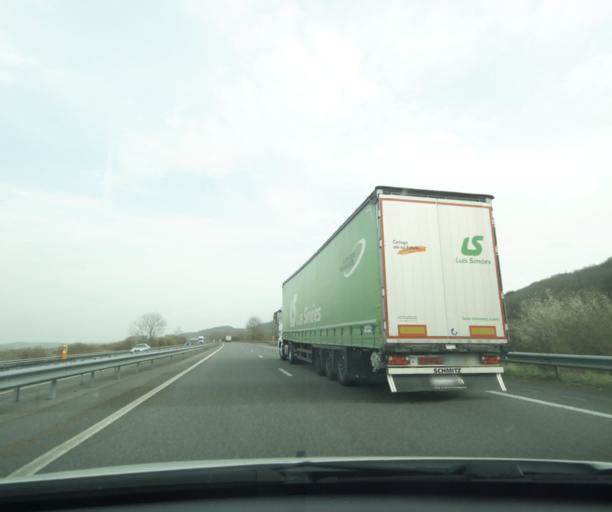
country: FR
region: Aquitaine
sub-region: Departement des Landes
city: Labatut
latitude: 43.5184
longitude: -0.9720
